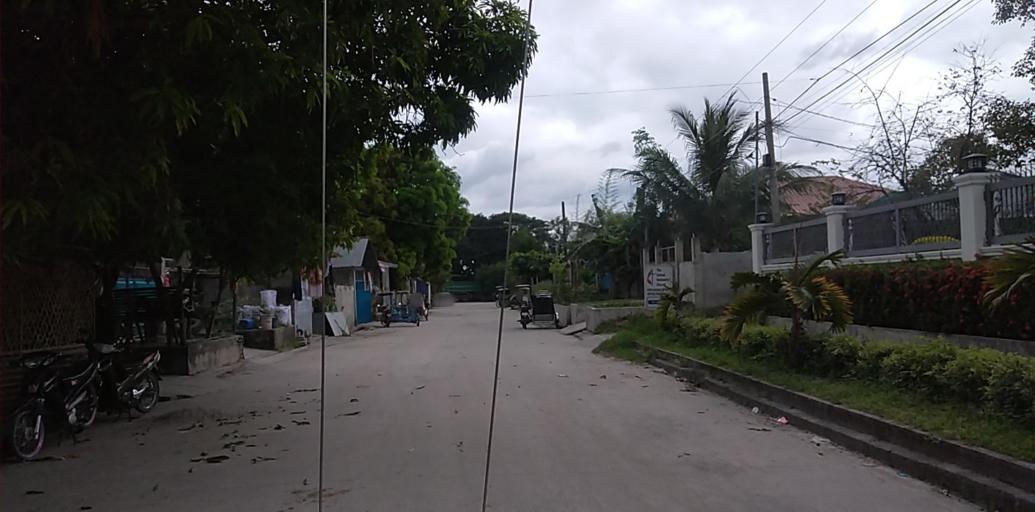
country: PH
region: Central Luzon
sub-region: Province of Pampanga
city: Pio
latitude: 15.0414
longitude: 120.5286
